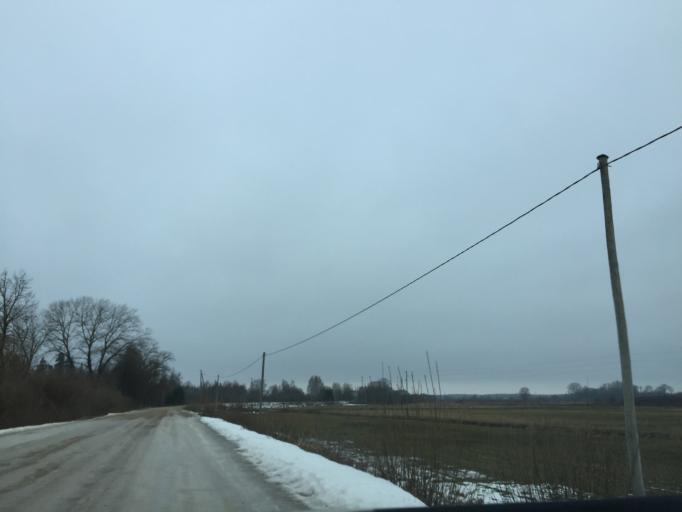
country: LV
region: Ozolnieku
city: Ozolnieki
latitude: 56.6315
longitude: 23.8091
